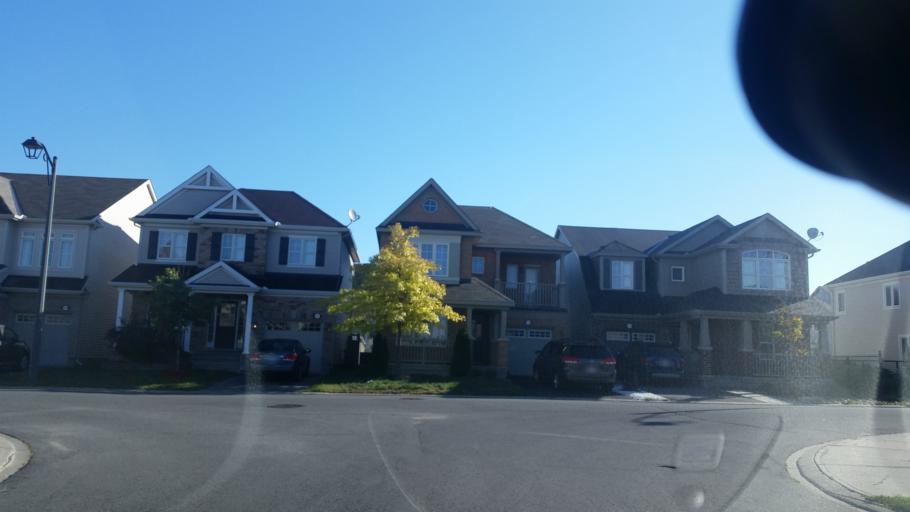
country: CA
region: Ontario
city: Bells Corners
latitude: 45.2512
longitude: -75.7447
